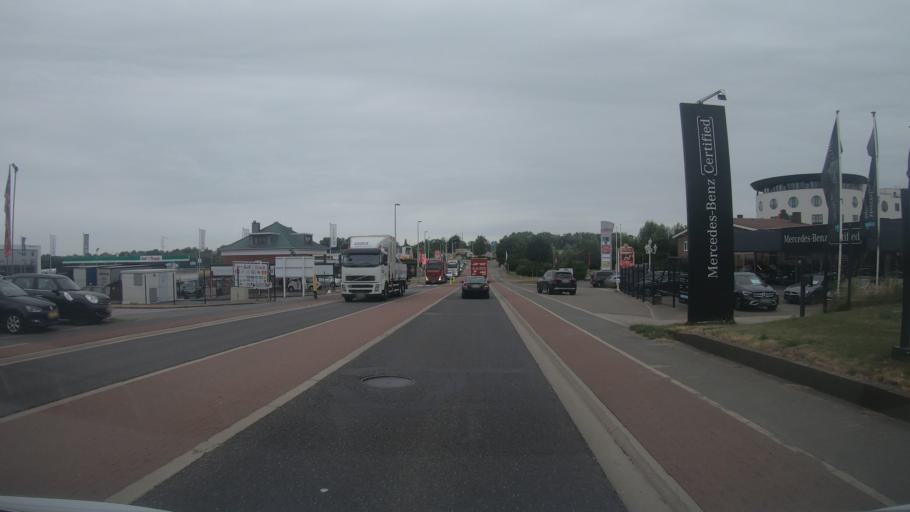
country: BE
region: Wallonia
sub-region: Province de Liege
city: Baelen
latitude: 50.6465
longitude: 6.0039
